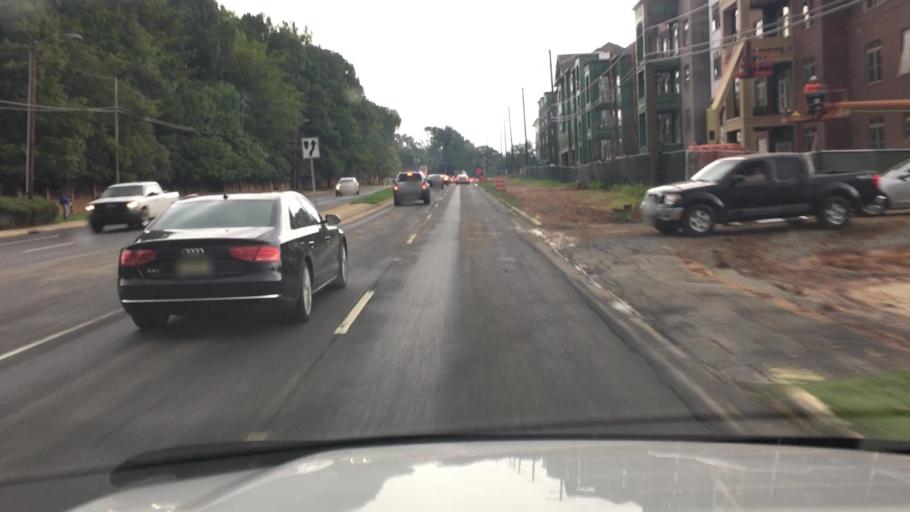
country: US
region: North Carolina
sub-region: Mecklenburg County
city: Charlotte
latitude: 35.1579
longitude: -80.7983
